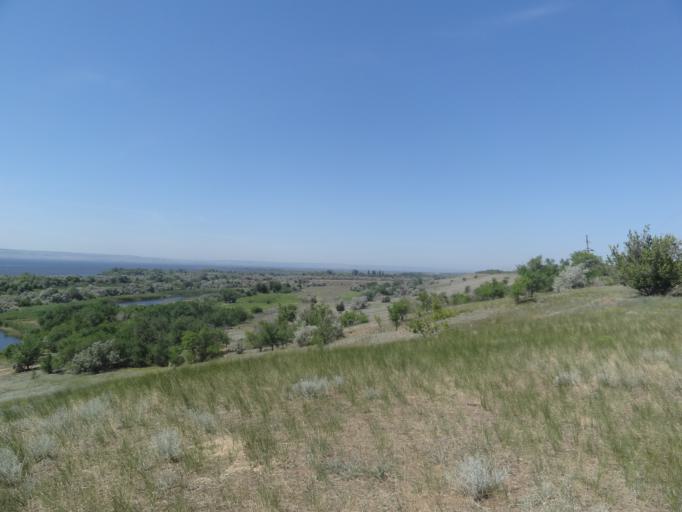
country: RU
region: Saratov
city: Krasnoarmeysk
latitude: 51.1293
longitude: 45.9401
